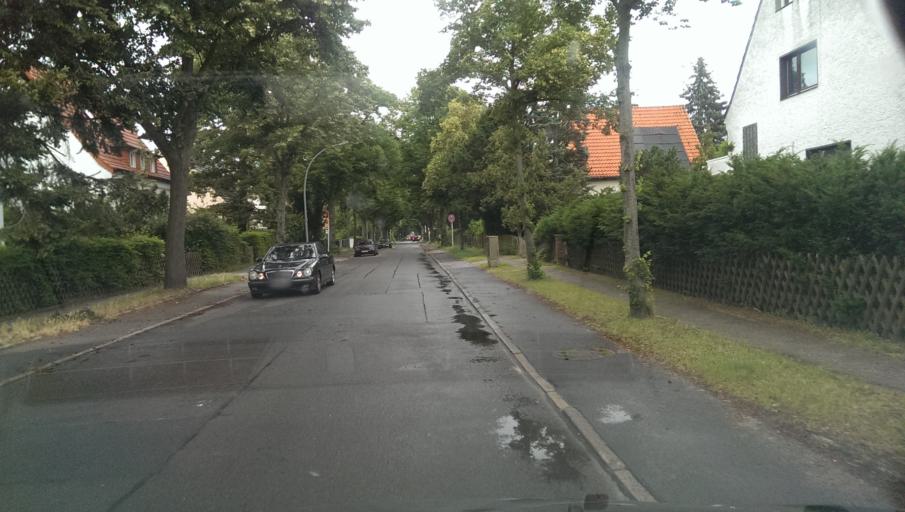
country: DE
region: Berlin
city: Zehlendorf Bezirk
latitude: 52.4249
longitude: 13.2414
